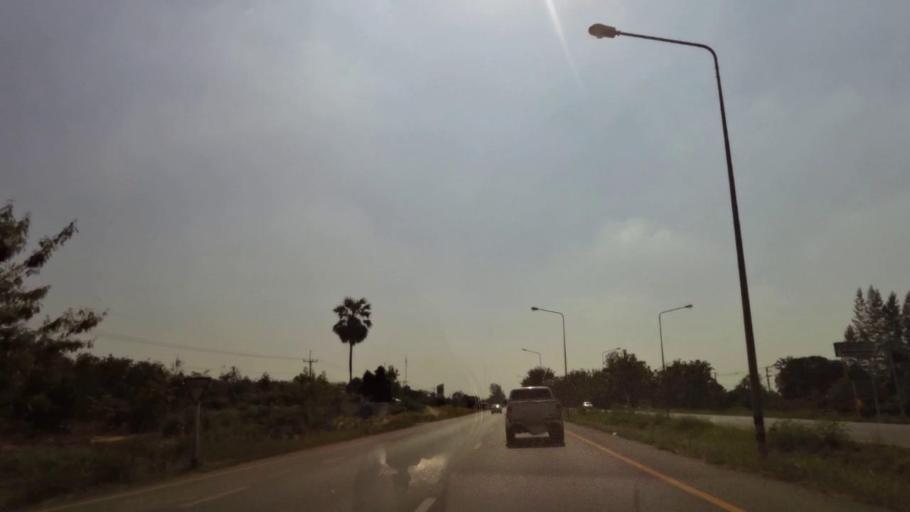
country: TH
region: Phichit
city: Wachira Barami
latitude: 16.4249
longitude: 100.1443
